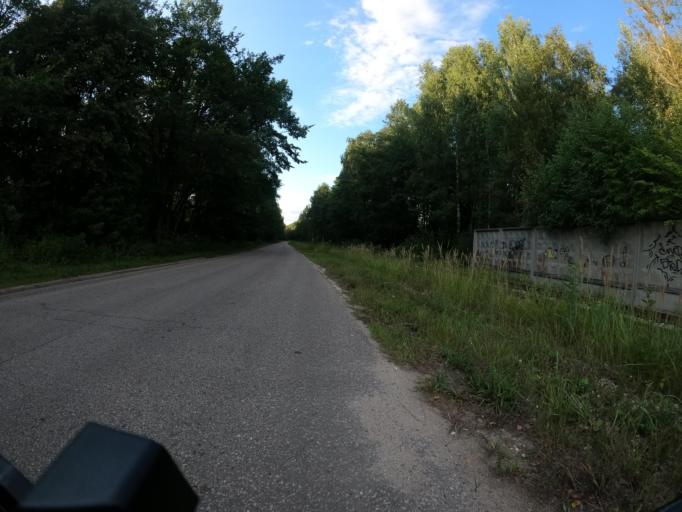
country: RU
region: Moskovskaya
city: Beloozerskiy
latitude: 55.4591
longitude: 38.4833
